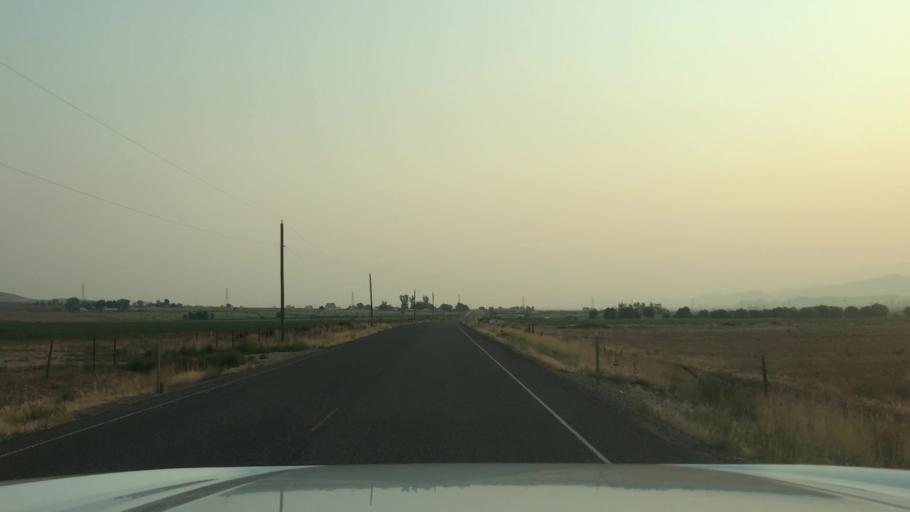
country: US
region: Utah
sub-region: Sevier County
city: Aurora
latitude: 38.8812
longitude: -111.9615
